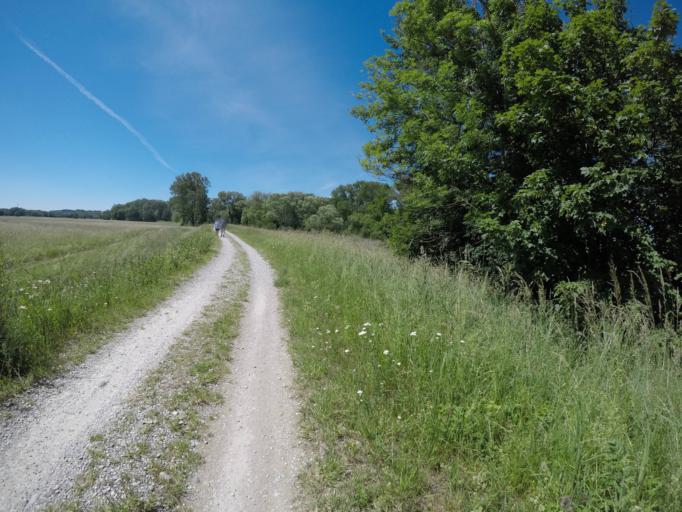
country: DE
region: Bavaria
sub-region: Upper Bavaria
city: Langenbach
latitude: 48.4593
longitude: 11.8878
